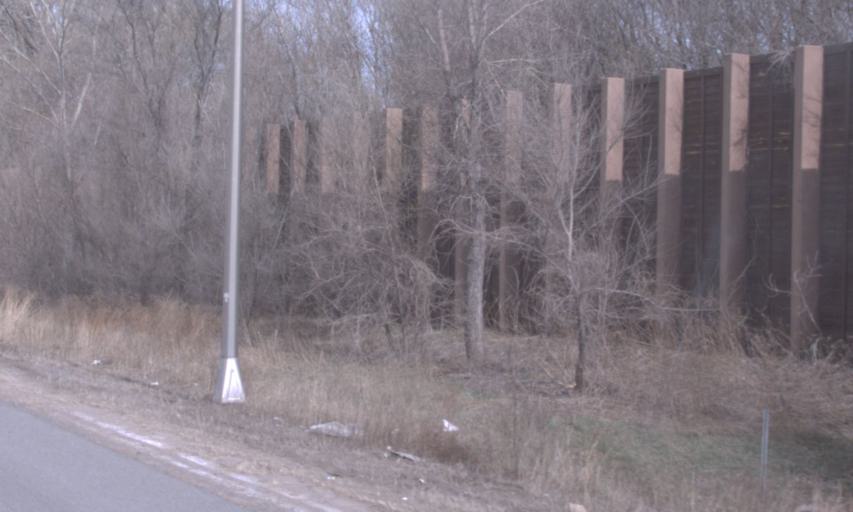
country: US
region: Minnesota
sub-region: Anoka County
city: Coon Rapids
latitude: 45.1639
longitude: -93.2858
